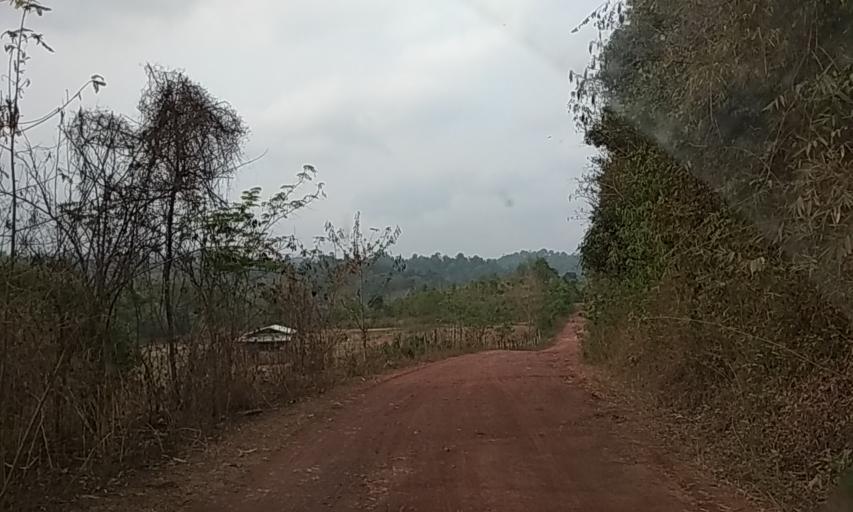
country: TH
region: Nan
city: Mae Charim
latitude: 18.4224
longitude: 101.1725
